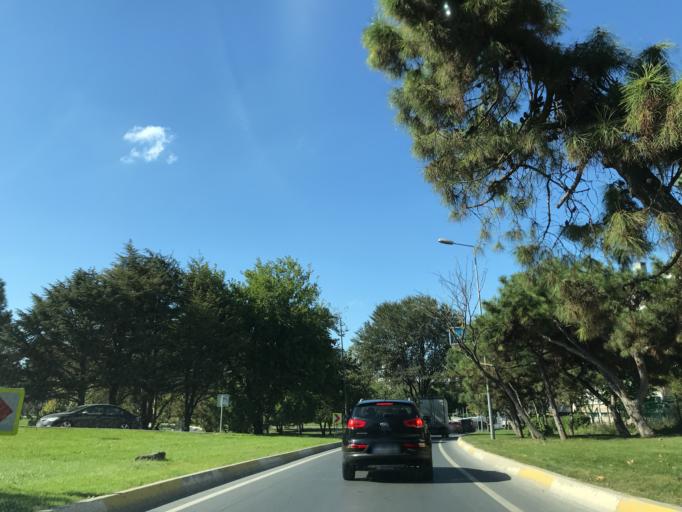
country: TR
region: Istanbul
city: Bahcelievler
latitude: 40.9757
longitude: 28.8674
